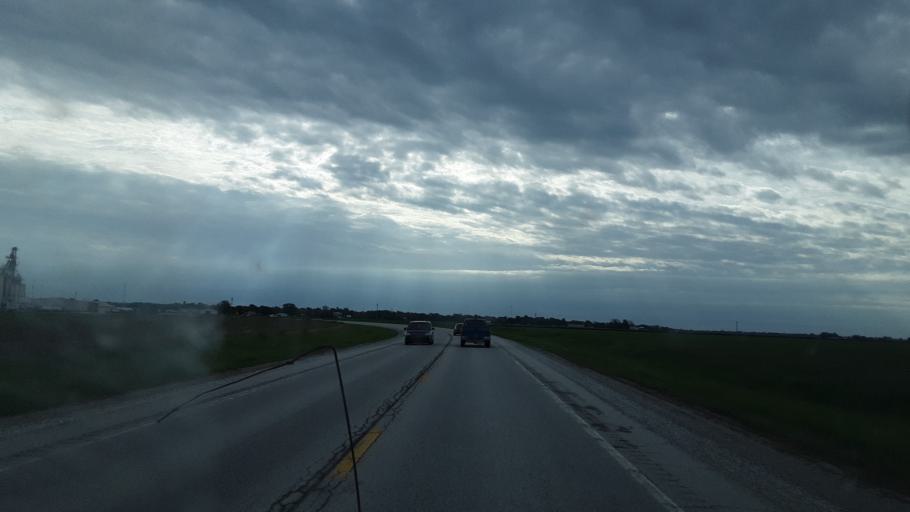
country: US
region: Illinois
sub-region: Hancock County
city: Carthage
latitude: 40.4093
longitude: -91.1644
